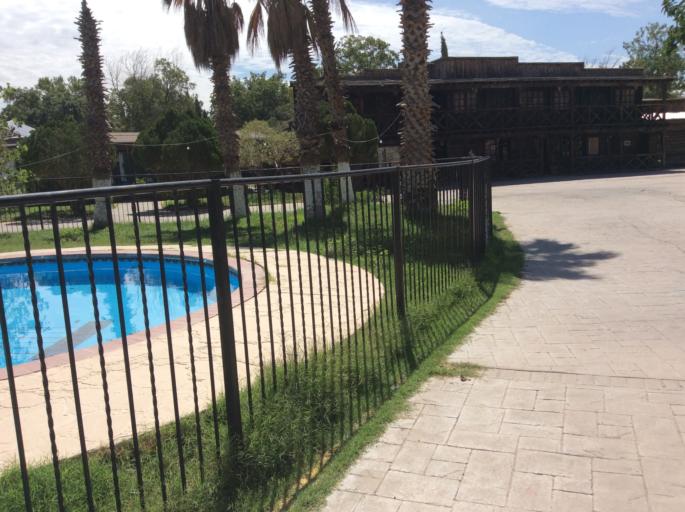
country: US
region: Texas
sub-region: El Paso County
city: Socorro
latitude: 31.6639
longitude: -106.3788
